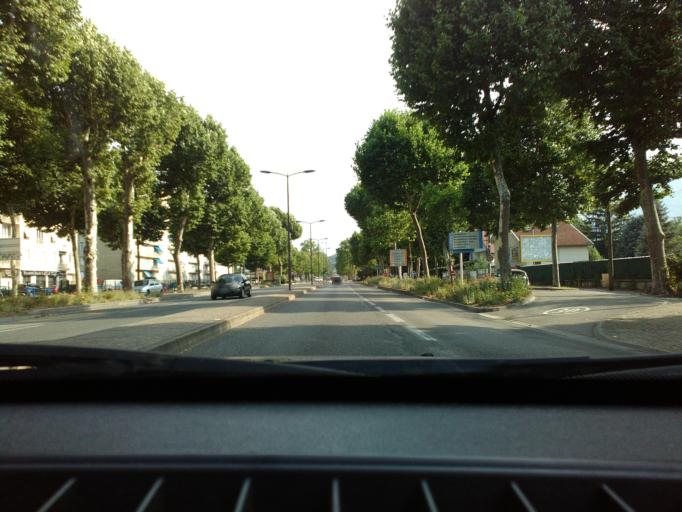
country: FR
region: Rhone-Alpes
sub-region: Departement de l'Isere
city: Le Pont-de-Claix
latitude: 45.1316
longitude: 5.7000
